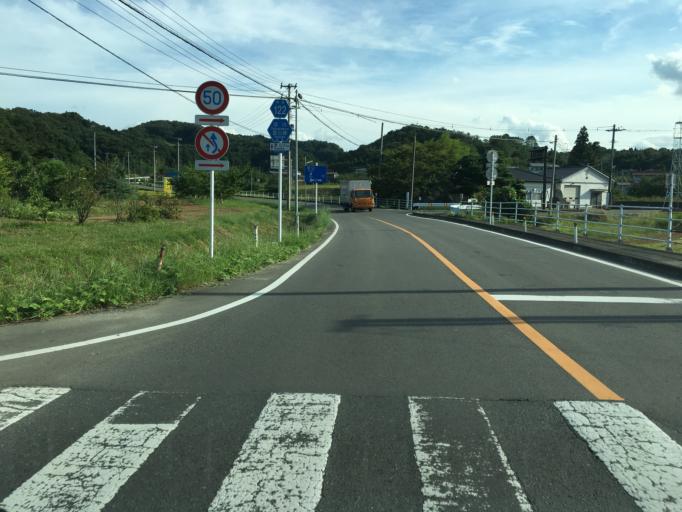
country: JP
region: Fukushima
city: Yanagawamachi-saiwaicho
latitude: 37.8188
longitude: 140.5874
